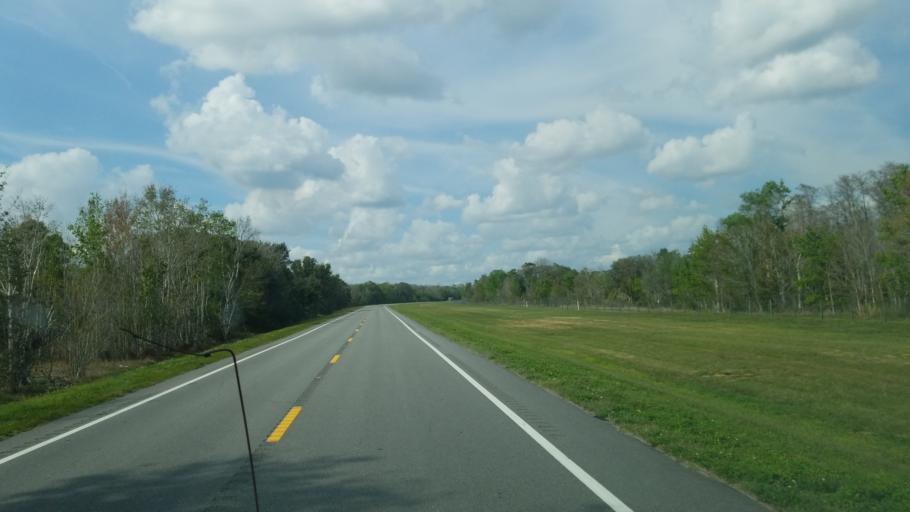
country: US
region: Florida
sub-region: Indian River County
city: Fellsmere
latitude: 27.7641
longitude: -80.9134
